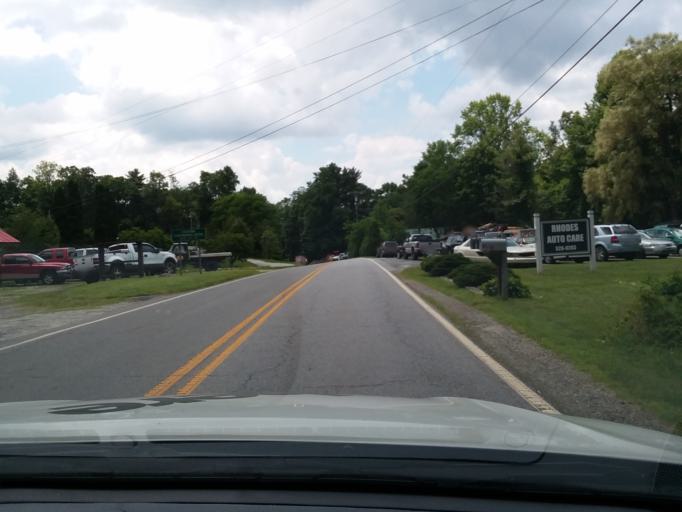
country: US
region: Georgia
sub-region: Rabun County
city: Mountain City
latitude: 35.0410
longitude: -83.2023
